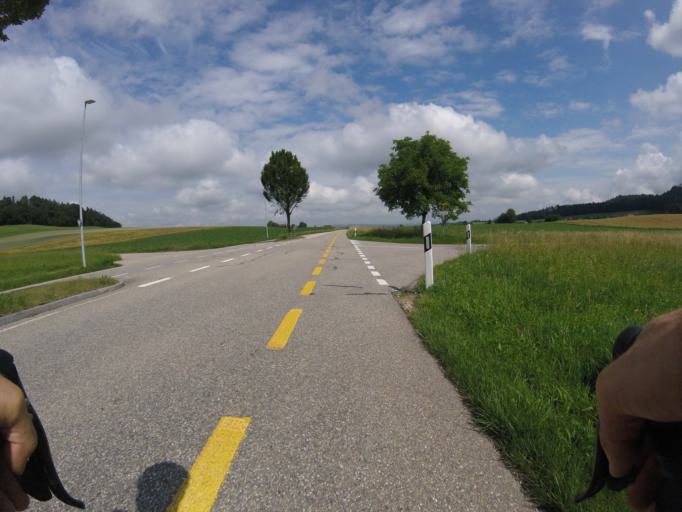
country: CH
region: Bern
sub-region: Emmental District
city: Krauchthal
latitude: 47.0251
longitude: 7.5535
